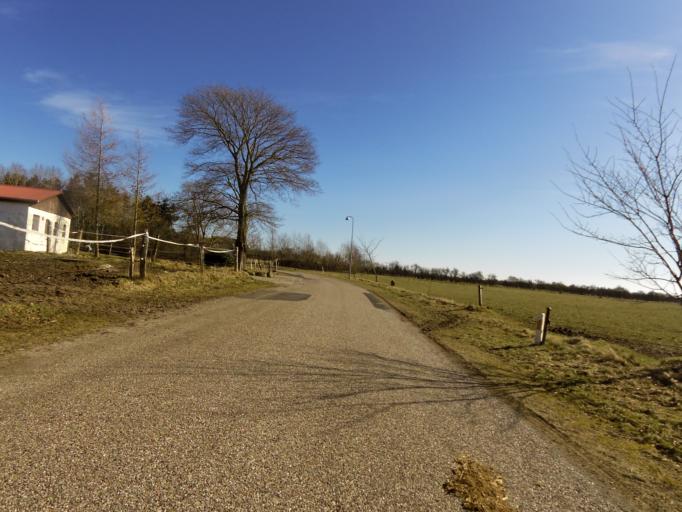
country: DK
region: South Denmark
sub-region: Tonder Kommune
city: Toftlund
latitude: 55.2326
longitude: 9.1285
